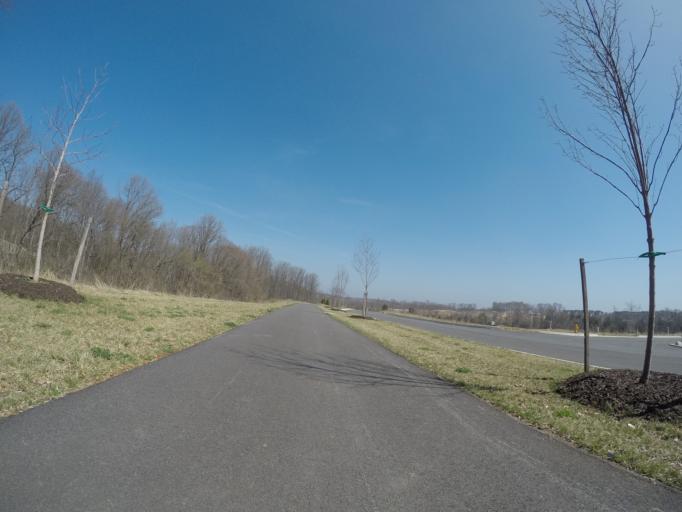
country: US
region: Maryland
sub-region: Frederick County
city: Green Valley
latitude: 39.3608
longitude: -77.2883
